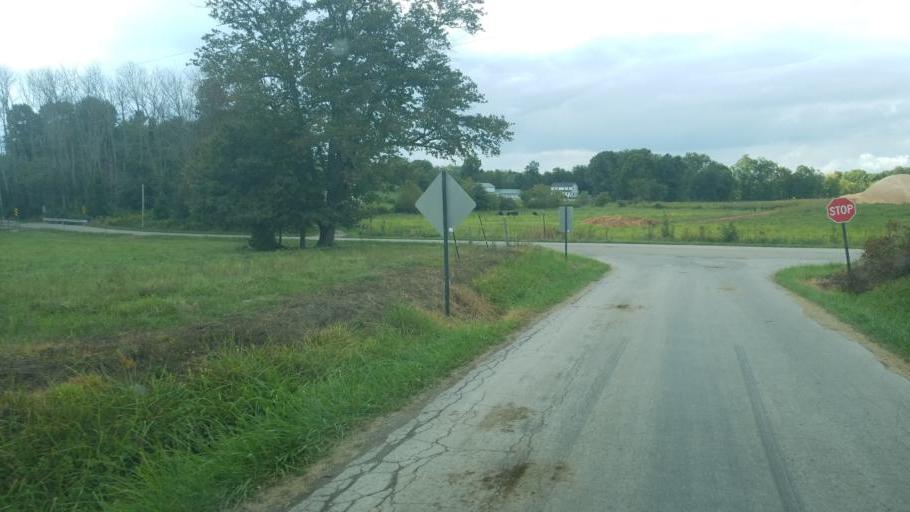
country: US
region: Ohio
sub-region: Jackson County
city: Oak Hill
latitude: 38.9446
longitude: -82.6294
